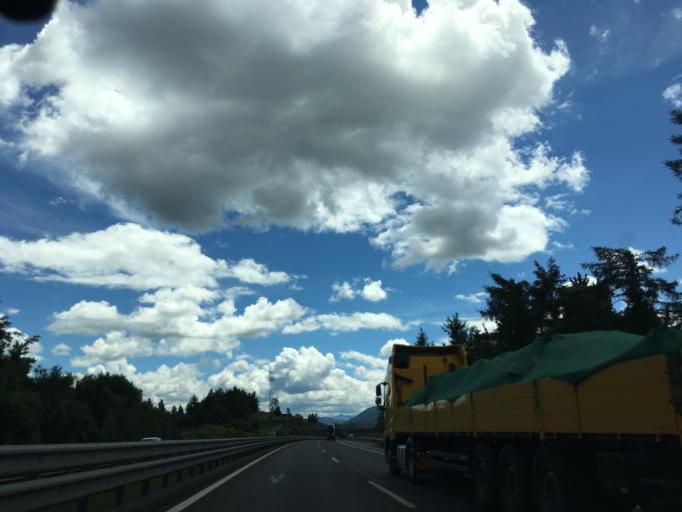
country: SI
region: Cerknica
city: Rakek
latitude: 45.8424
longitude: 14.2918
